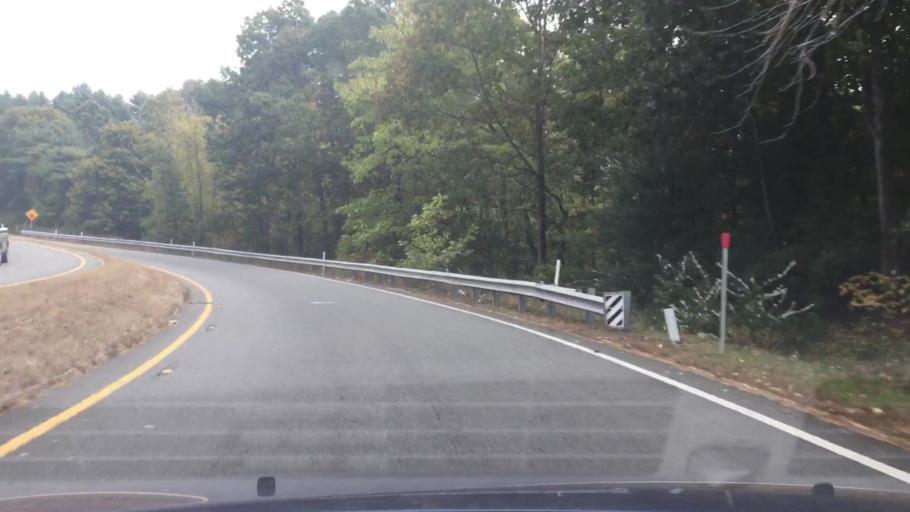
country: US
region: Massachusetts
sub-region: Essex County
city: Haverhill
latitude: 42.7988
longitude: -71.0959
